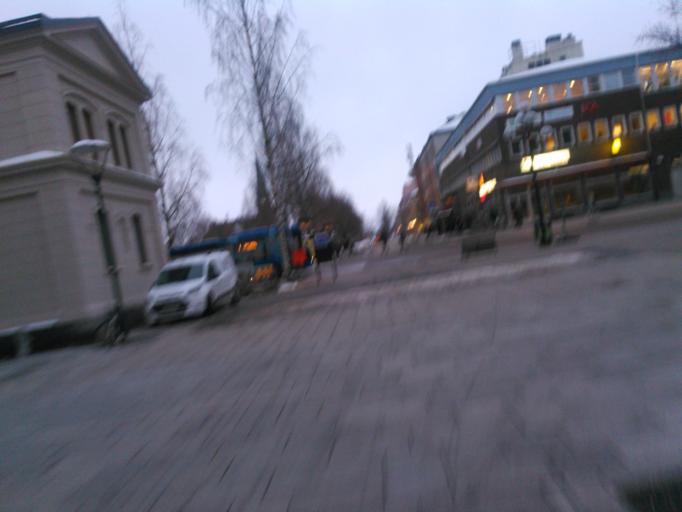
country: SE
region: Vaesterbotten
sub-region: Umea Kommun
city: Umea
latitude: 63.8262
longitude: 20.2690
